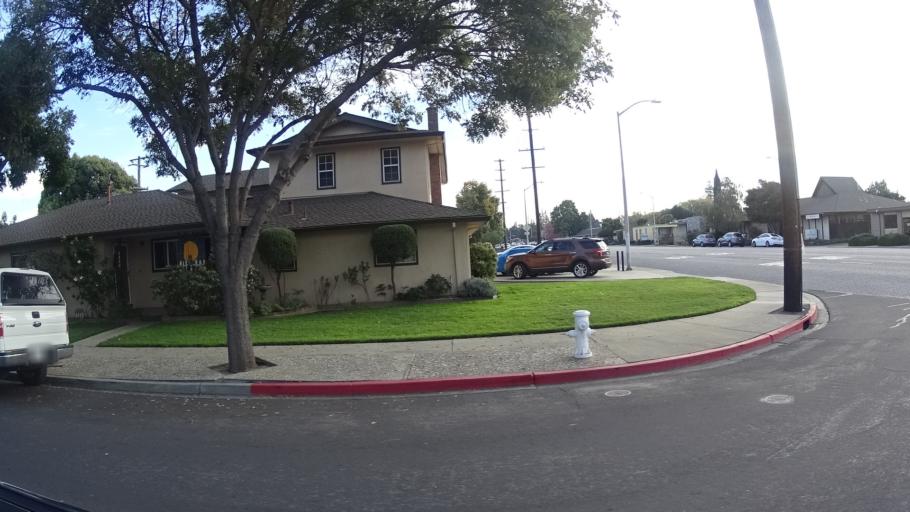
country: US
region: California
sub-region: Santa Clara County
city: Santa Clara
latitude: 37.3493
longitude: -121.9592
